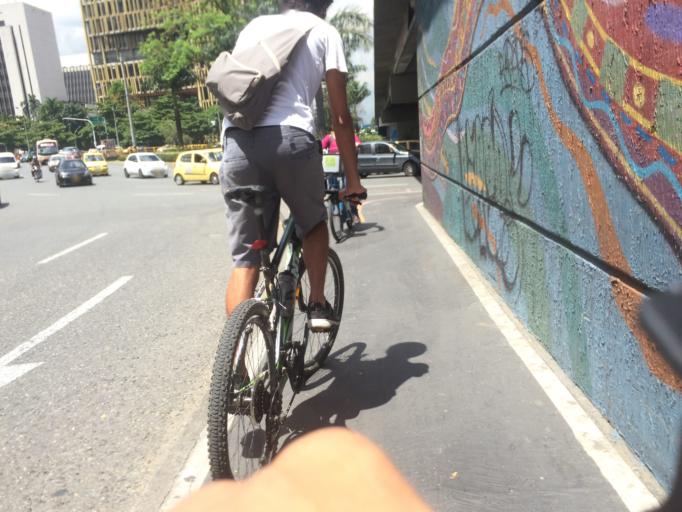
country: CO
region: Antioquia
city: Medellin
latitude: 6.2470
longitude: -75.5750
